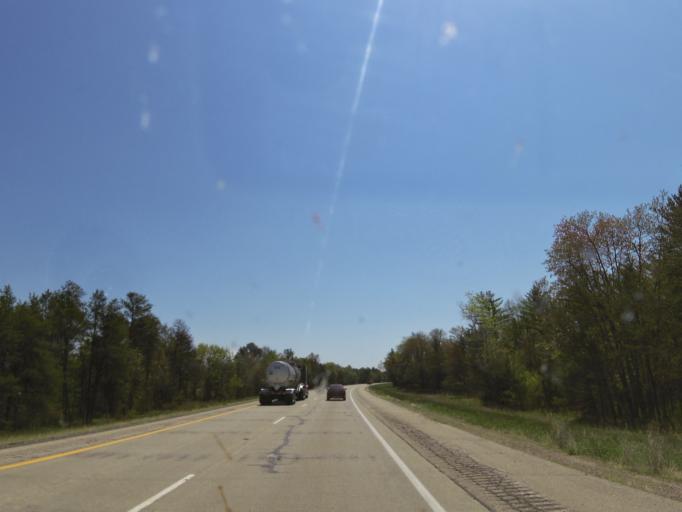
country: US
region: Wisconsin
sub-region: Monroe County
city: Tomah
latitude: 44.1827
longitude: -90.6168
